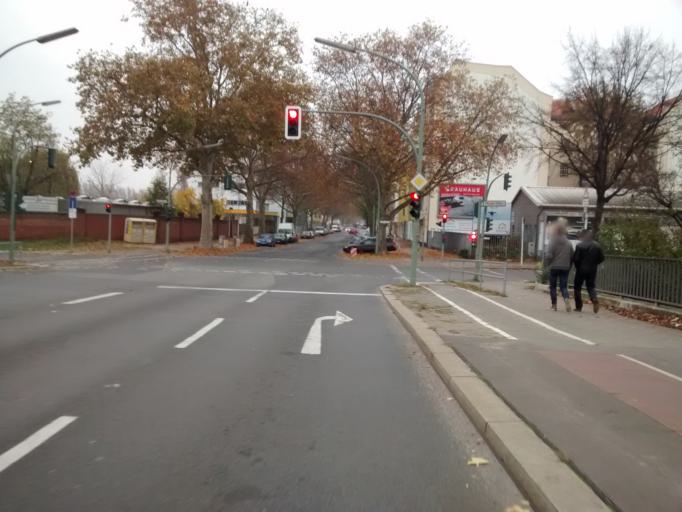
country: DE
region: Berlin
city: Charlottenburg-Nord
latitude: 52.5302
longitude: 13.3139
